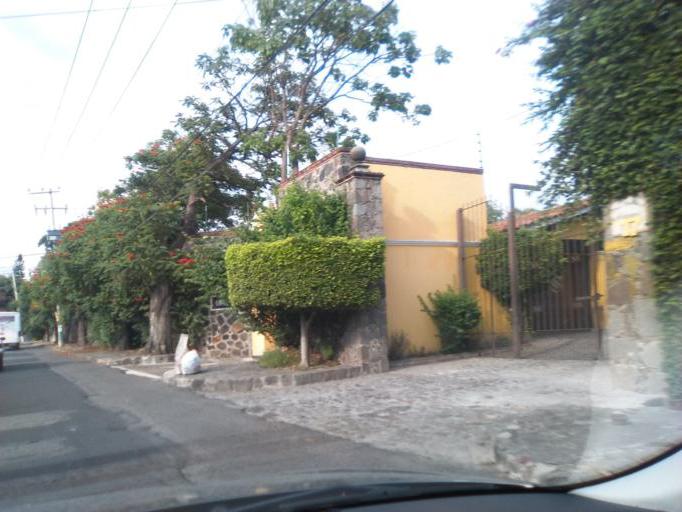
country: MX
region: Morelos
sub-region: Cuernavaca
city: Cuernavaca
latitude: 18.9080
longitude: -99.2279
